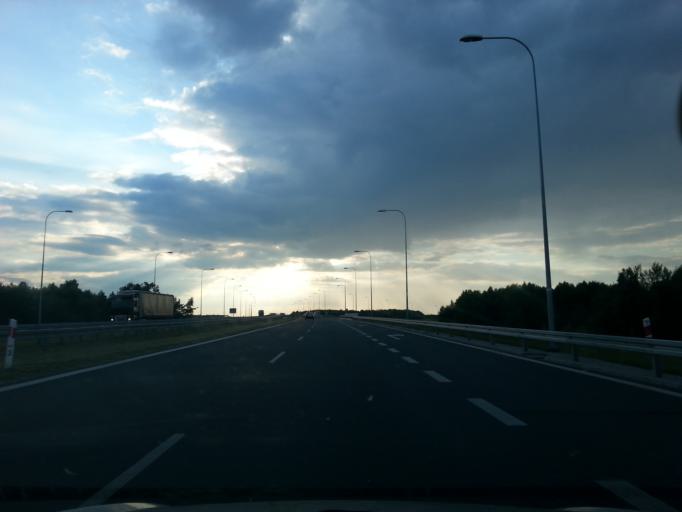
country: PL
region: Lodz Voivodeship
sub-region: Powiat zdunskowolski
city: Zapolice
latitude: 51.5960
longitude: 18.8802
